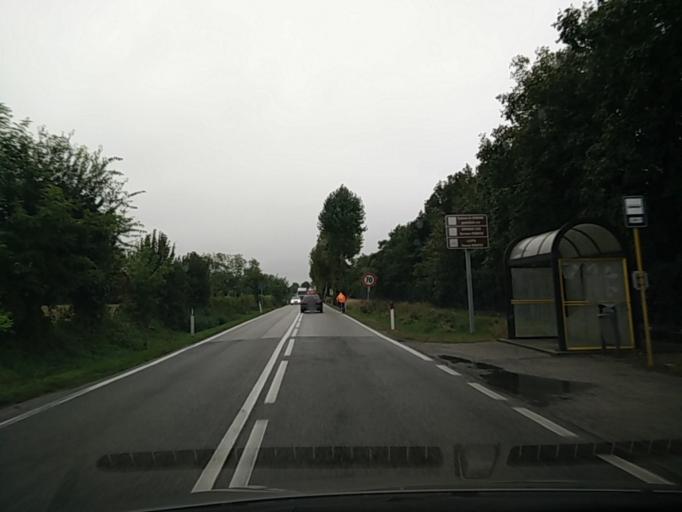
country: IT
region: Veneto
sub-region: Provincia di Treviso
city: Ospedaletto
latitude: 45.6804
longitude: 12.0777
